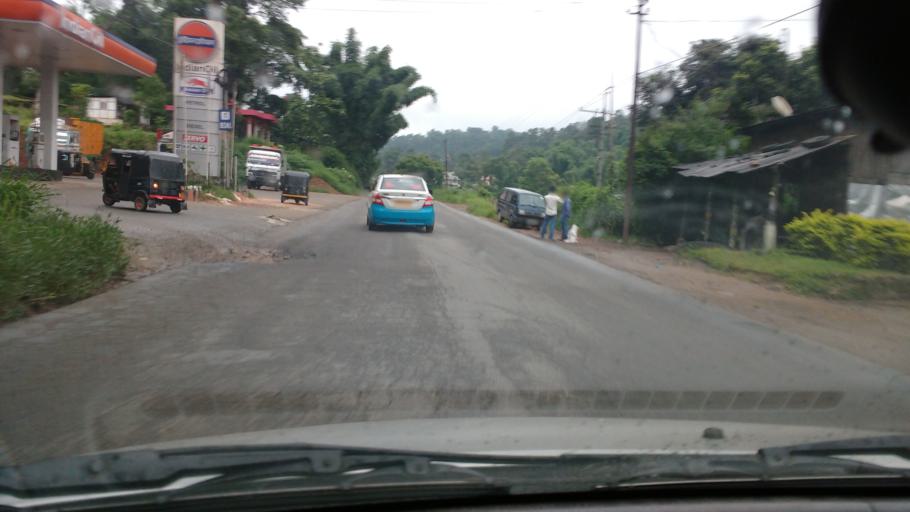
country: IN
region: Meghalaya
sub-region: Ri-Bhoi
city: Nongpoh
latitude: 25.7406
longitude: 91.8879
